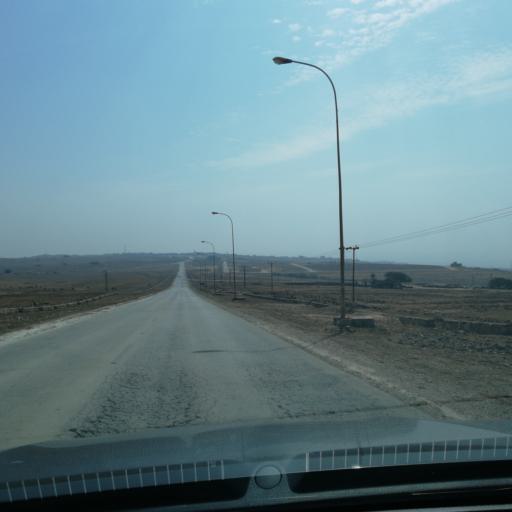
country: OM
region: Zufar
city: Salalah
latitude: 17.2398
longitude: 54.0578
